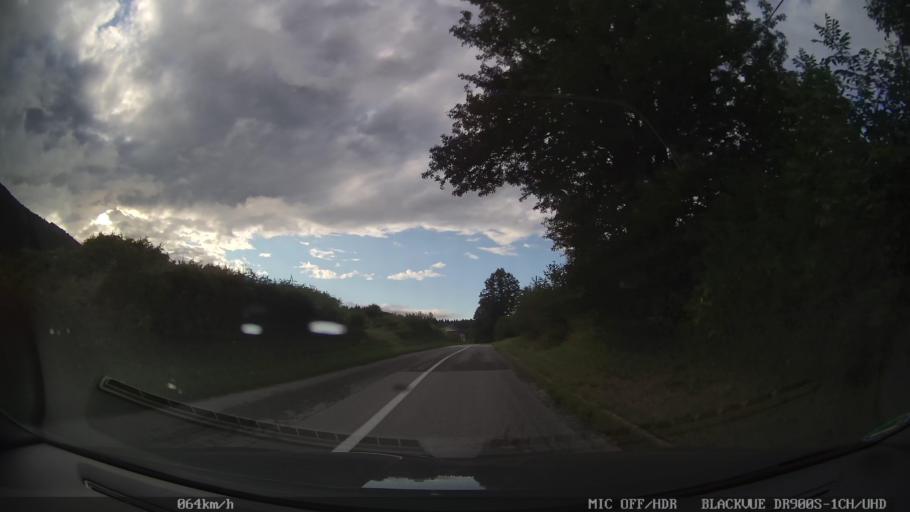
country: HR
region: Karlovacka
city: Plaski
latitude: 44.9948
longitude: 15.4272
